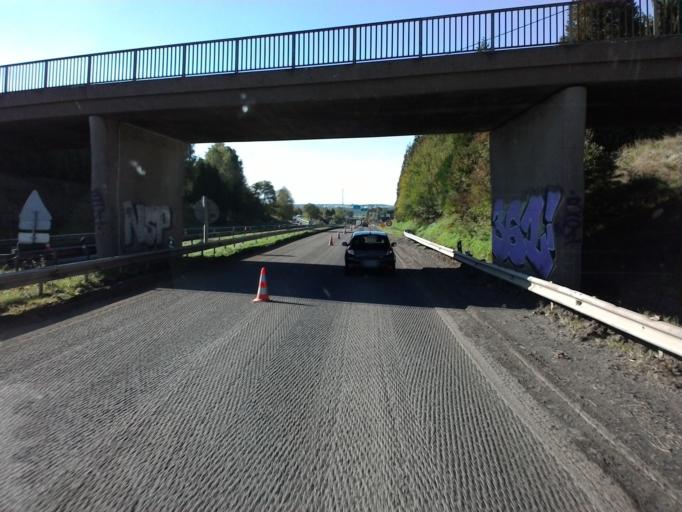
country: FR
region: Lorraine
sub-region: Departement de Meurthe-et-Moselle
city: Haucourt-Moulaine
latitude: 49.5016
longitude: 5.7955
